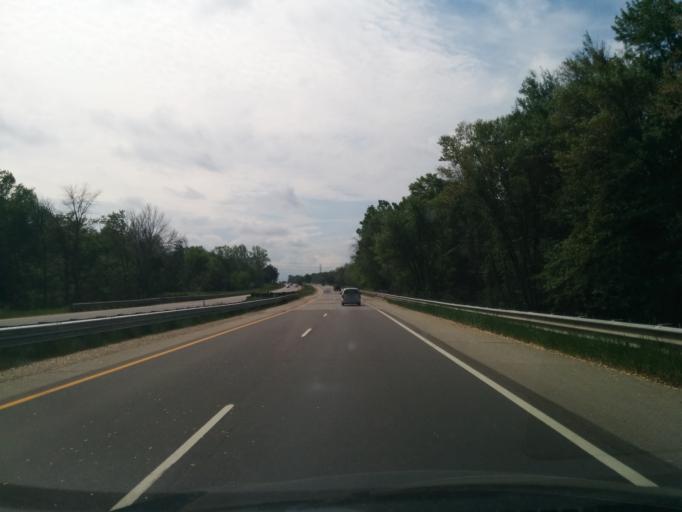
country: US
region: Michigan
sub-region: Ottawa County
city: Beechwood
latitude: 42.9167
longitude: -86.1449
